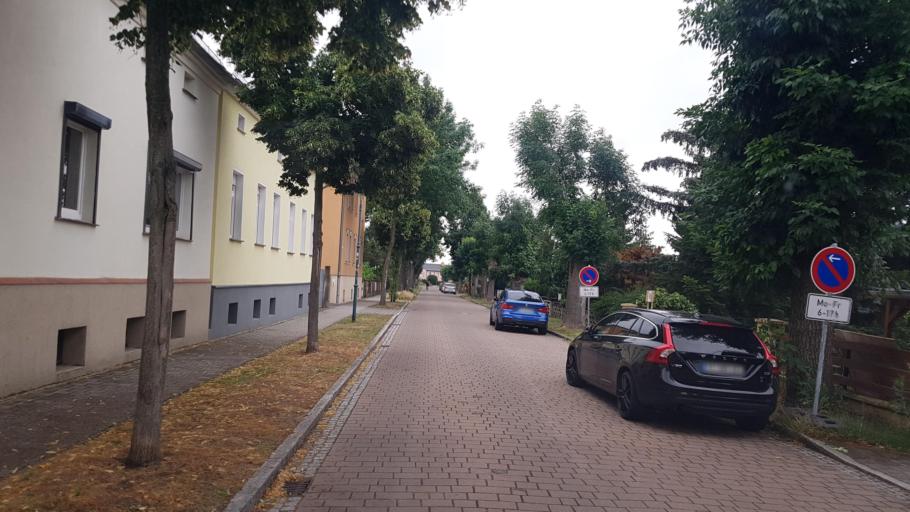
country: DE
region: Brandenburg
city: Trebbin
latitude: 52.2157
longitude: 13.2186
